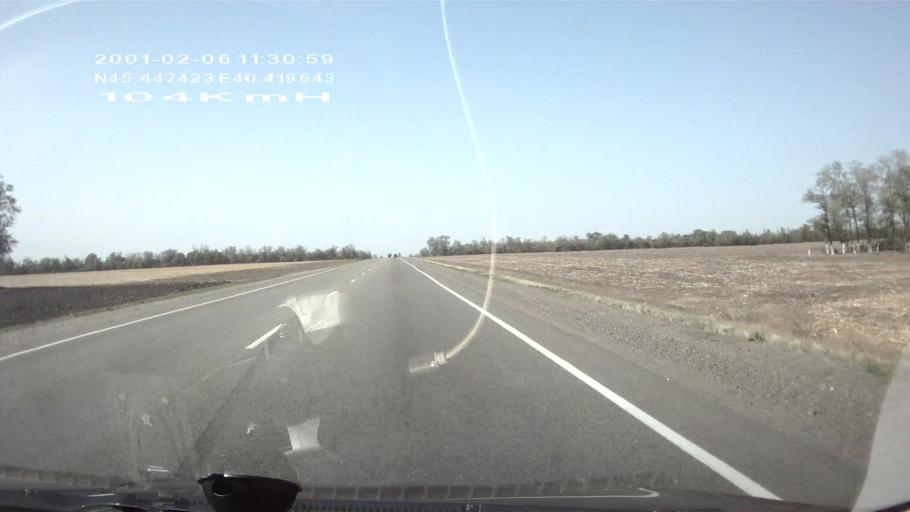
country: RU
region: Krasnodarskiy
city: Kazanskaya
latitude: 45.4474
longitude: 40.4177
